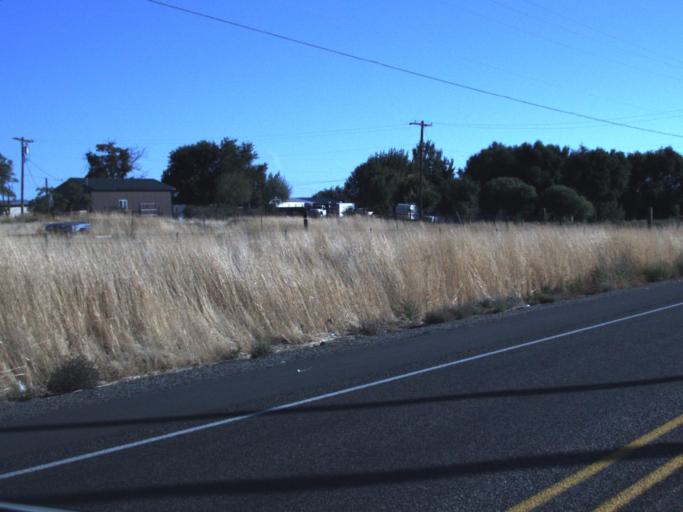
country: US
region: Washington
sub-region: Benton County
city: Finley
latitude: 46.1894
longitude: -119.0755
